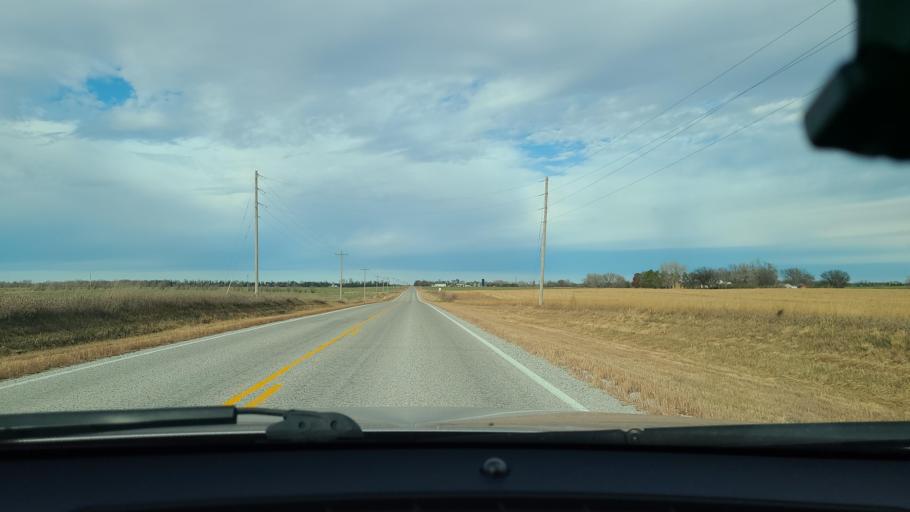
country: US
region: Kansas
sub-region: McPherson County
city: Inman
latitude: 38.3002
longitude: -97.9249
